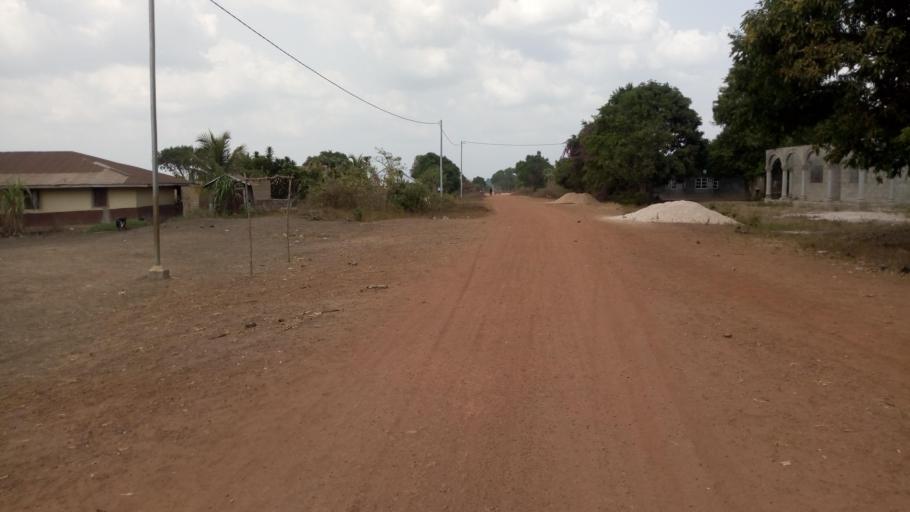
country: SL
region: Southern Province
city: Mogbwemo
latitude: 7.7890
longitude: -12.3064
